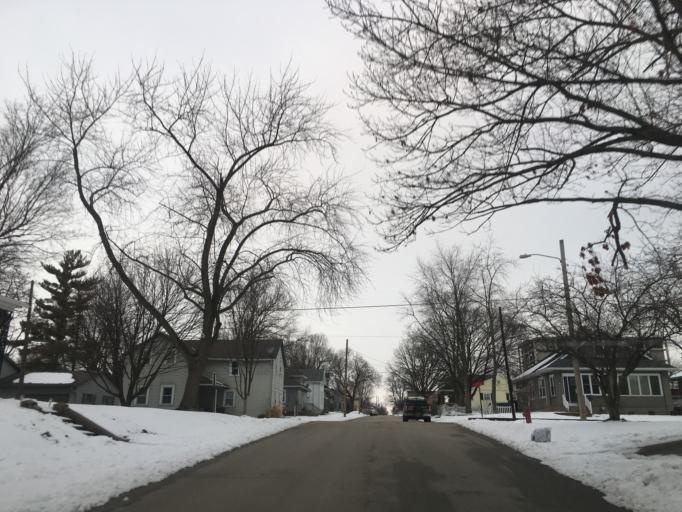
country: US
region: Illinois
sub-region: LaSalle County
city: Peru
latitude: 41.3255
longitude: -89.1344
